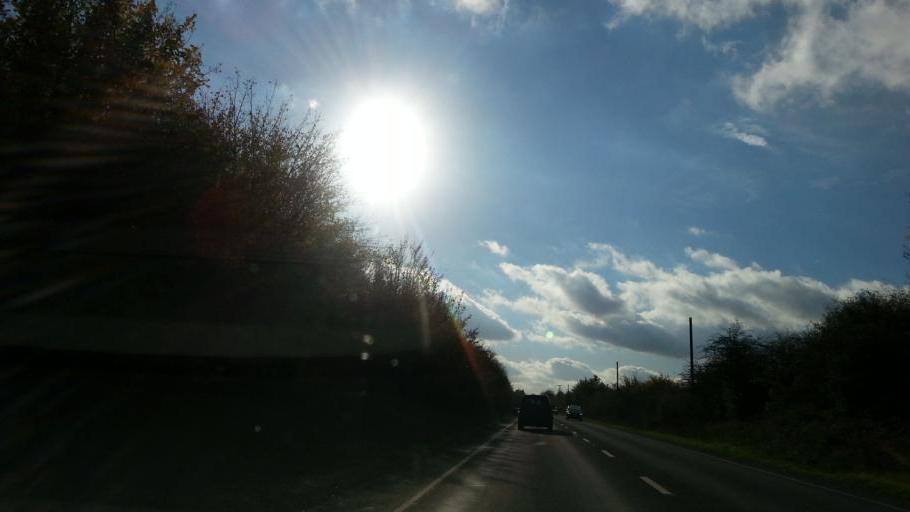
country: GB
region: England
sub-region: Norfolk
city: Harleston
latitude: 52.3803
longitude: 1.2566
